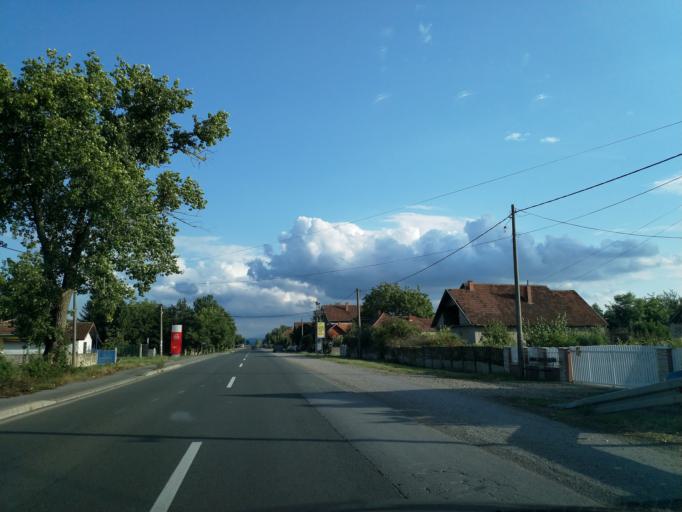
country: RS
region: Central Serbia
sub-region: Pomoravski Okrug
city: Paracin
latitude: 43.8054
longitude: 21.4213
